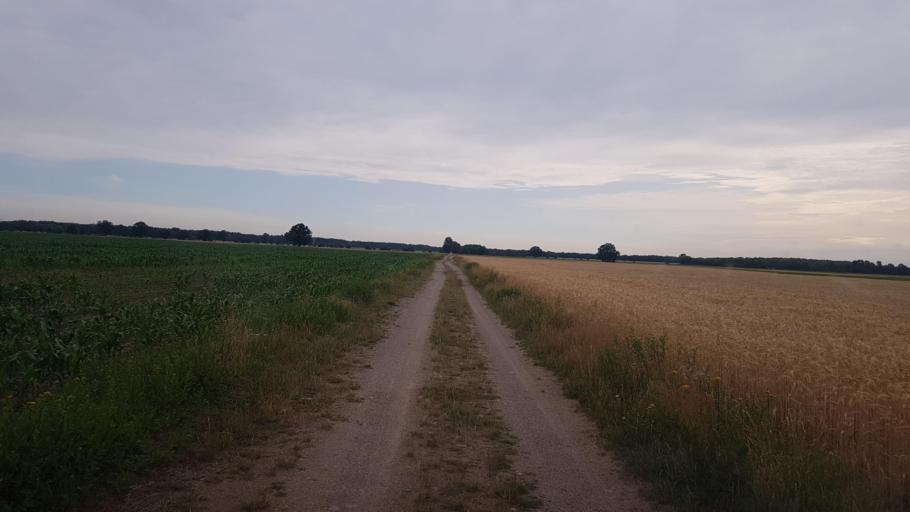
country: DE
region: Saxony-Anhalt
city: Holzdorf
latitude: 51.7465
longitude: 13.1769
